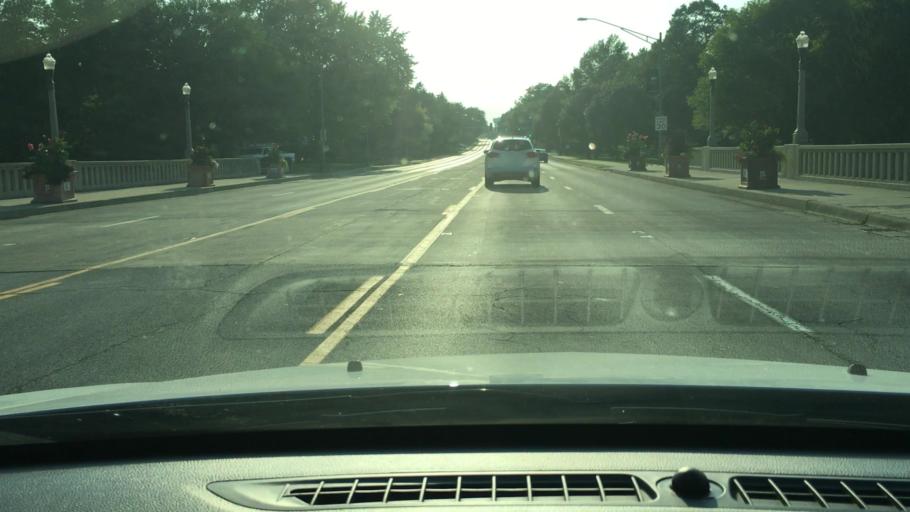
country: US
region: Illinois
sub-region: DeKalb County
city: DeKalb
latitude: 41.9310
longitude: -88.7592
